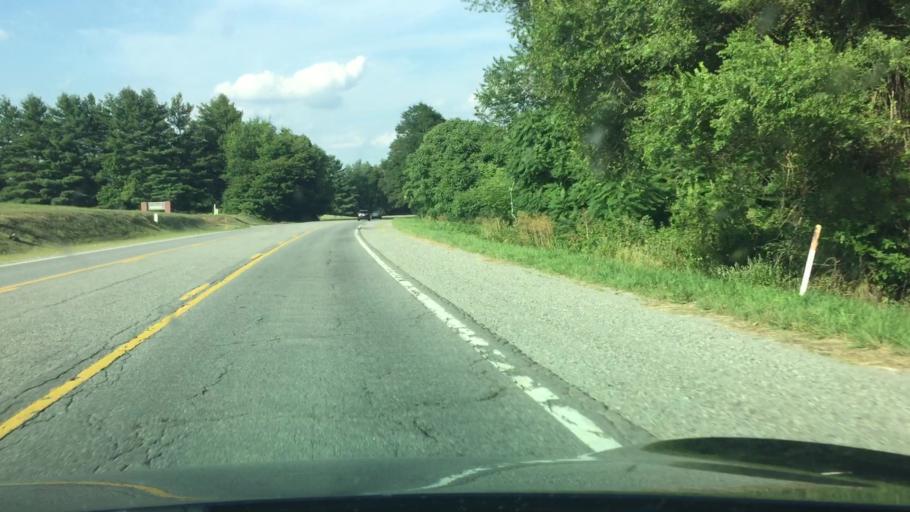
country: US
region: Virginia
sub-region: Pulaski County
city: Dublin
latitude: 37.1164
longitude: -80.6680
